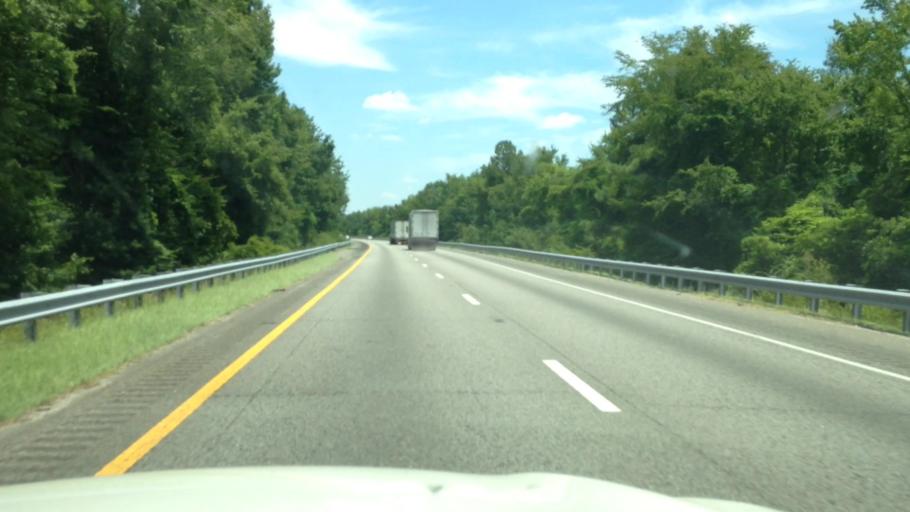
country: US
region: South Carolina
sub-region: Florence County
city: Florence
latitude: 34.2885
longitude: -79.6570
